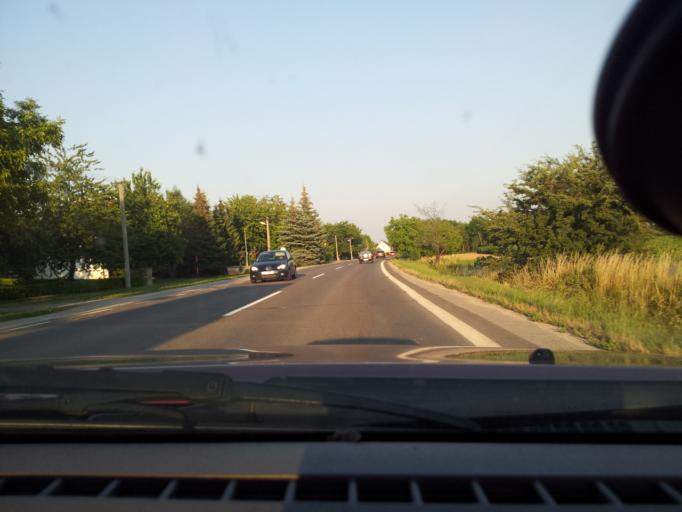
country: SK
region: Trnavsky
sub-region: Okres Skalica
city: Skalica
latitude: 48.7729
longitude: 17.2708
